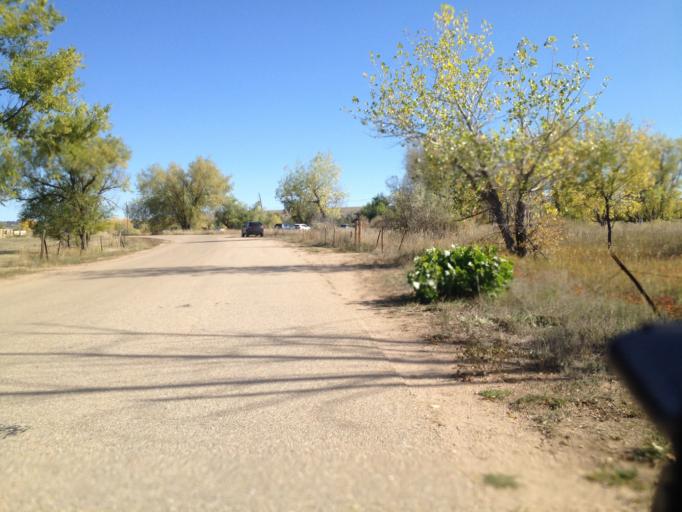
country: US
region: Colorado
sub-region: Boulder County
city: Boulder
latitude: 39.9832
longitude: -105.2344
